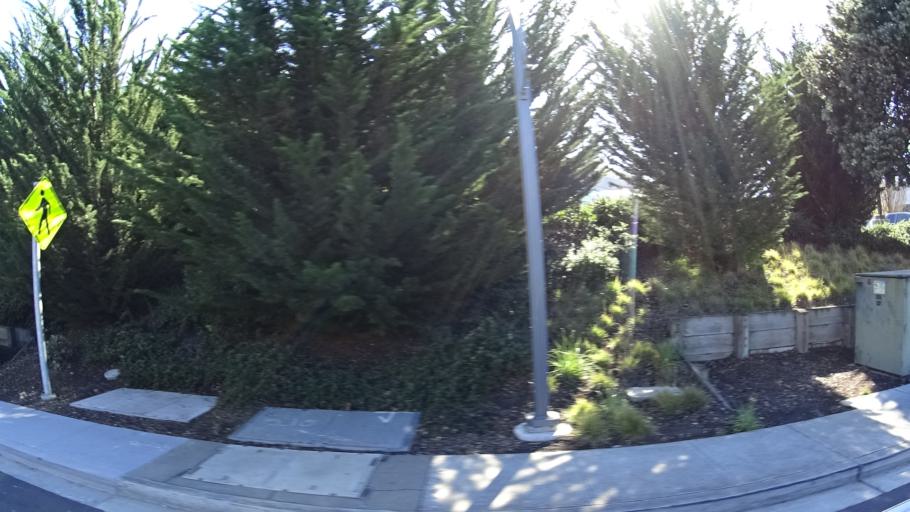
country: US
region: California
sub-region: San Mateo County
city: South San Francisco
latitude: 37.6554
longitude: -122.3842
